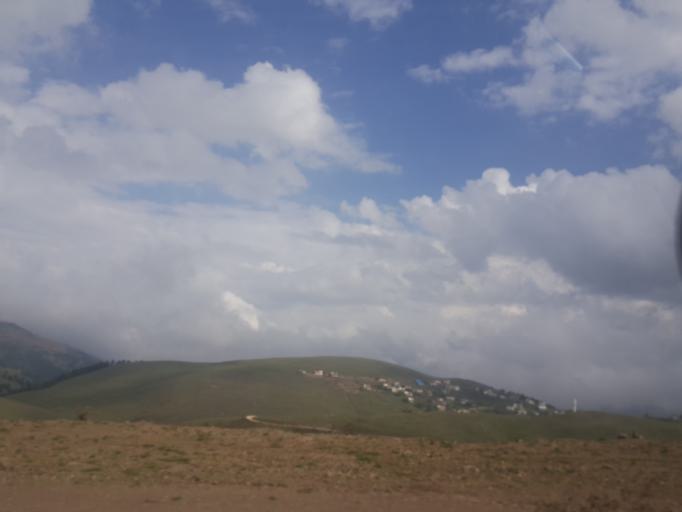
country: TR
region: Tokat
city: Bereketli
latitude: 40.5811
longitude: 37.3029
